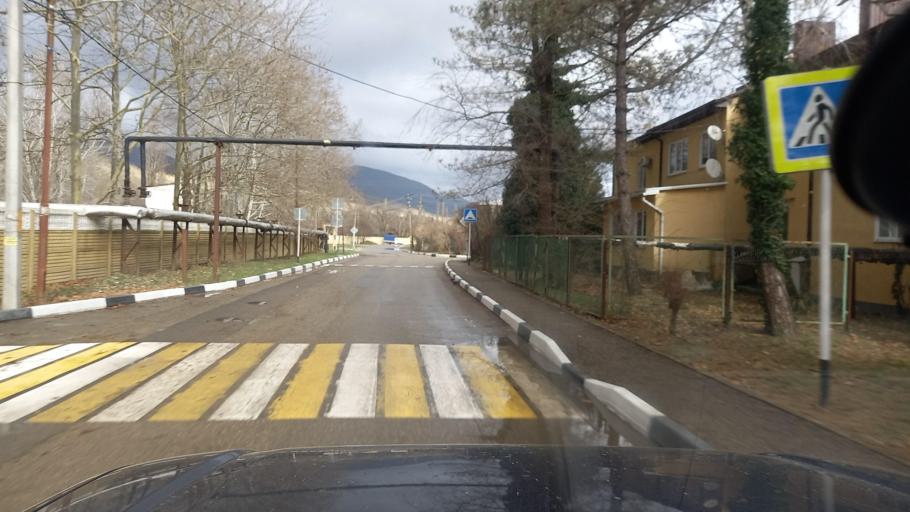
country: RU
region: Krasnodarskiy
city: Pshada
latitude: 44.4761
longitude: 38.3992
